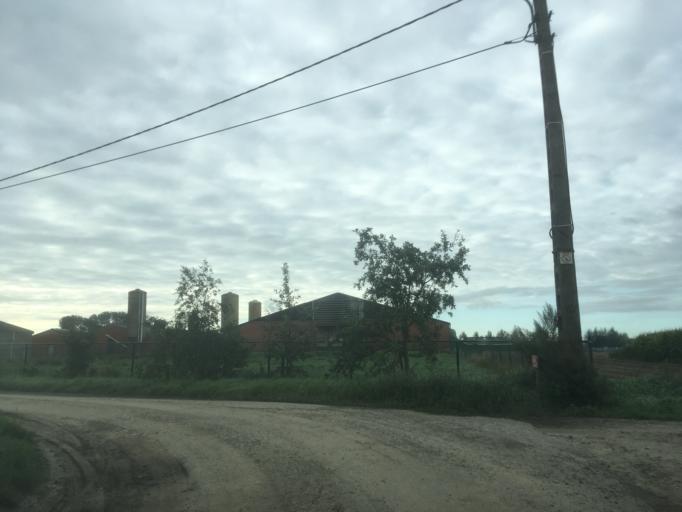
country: BE
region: Flanders
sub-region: Provincie West-Vlaanderen
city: Ardooie
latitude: 51.0173
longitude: 3.2204
